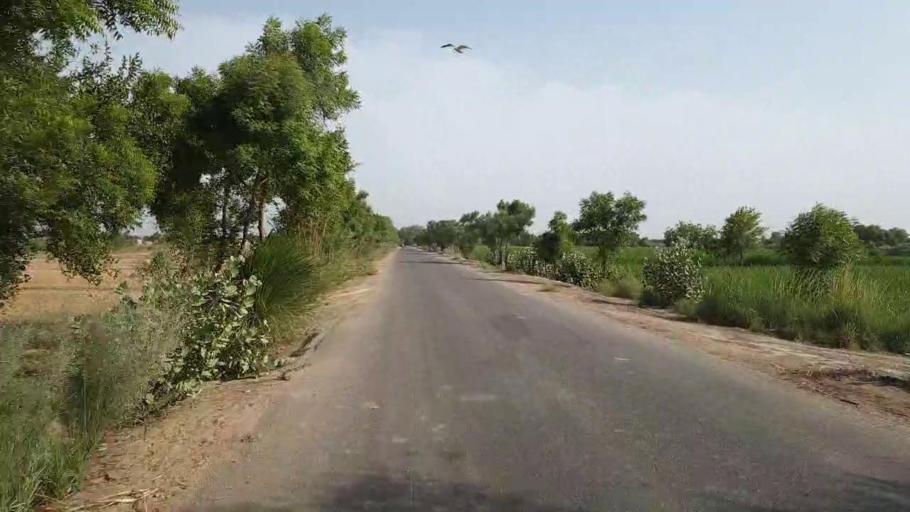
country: PK
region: Sindh
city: Sakrand
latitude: 26.2558
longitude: 68.2848
